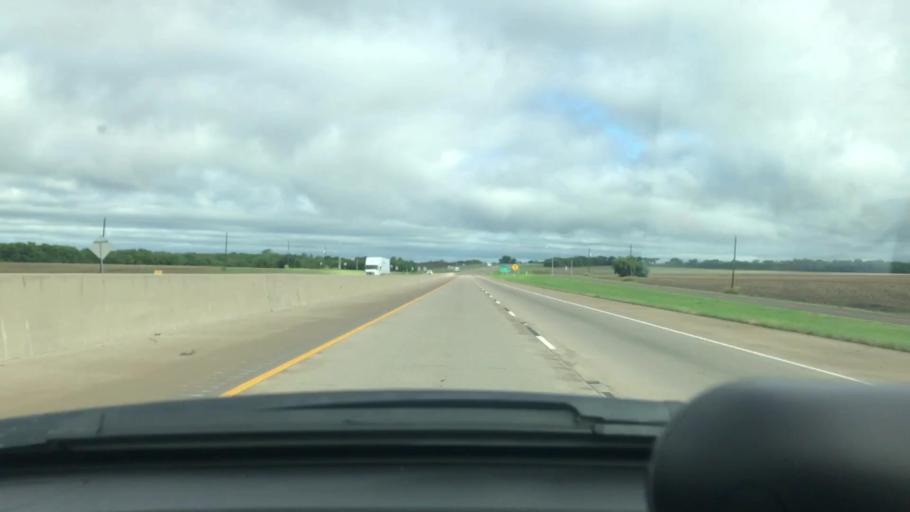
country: US
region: Texas
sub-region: Grayson County
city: Howe
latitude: 33.4678
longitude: -96.6142
